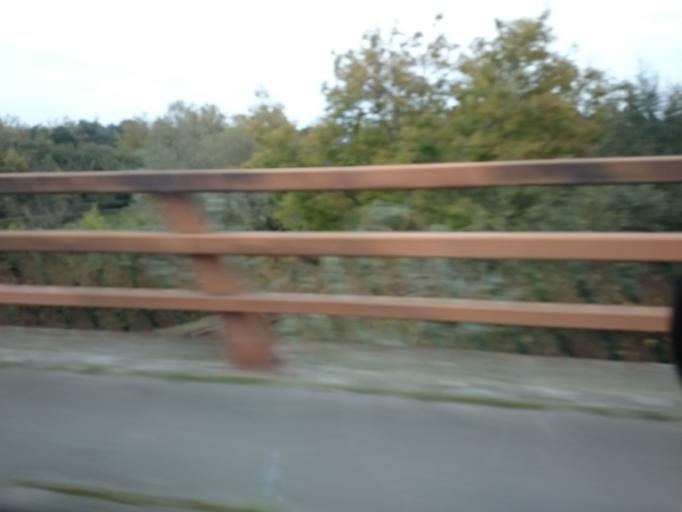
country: FR
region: Pays de la Loire
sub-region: Departement de la Loire-Atlantique
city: Indre
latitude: 47.2066
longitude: -1.6668
